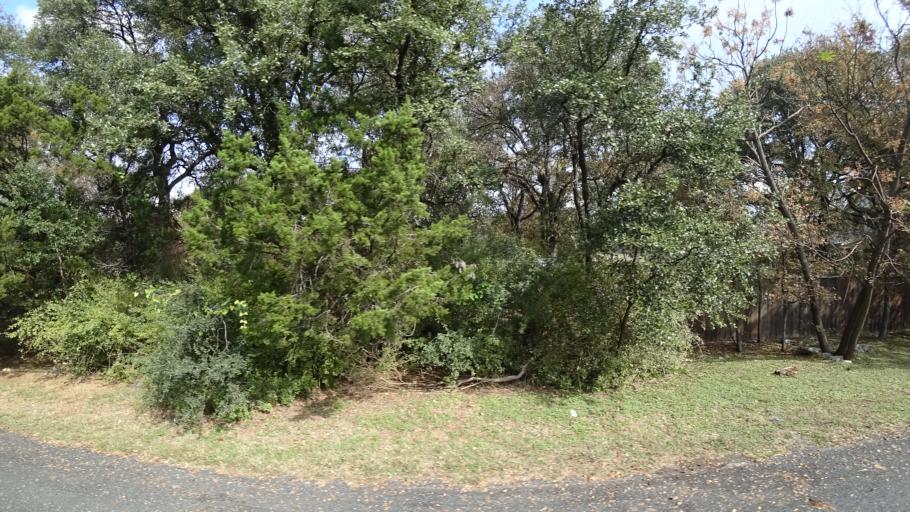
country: US
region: Texas
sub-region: Travis County
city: Wells Branch
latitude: 30.4341
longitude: -97.7096
